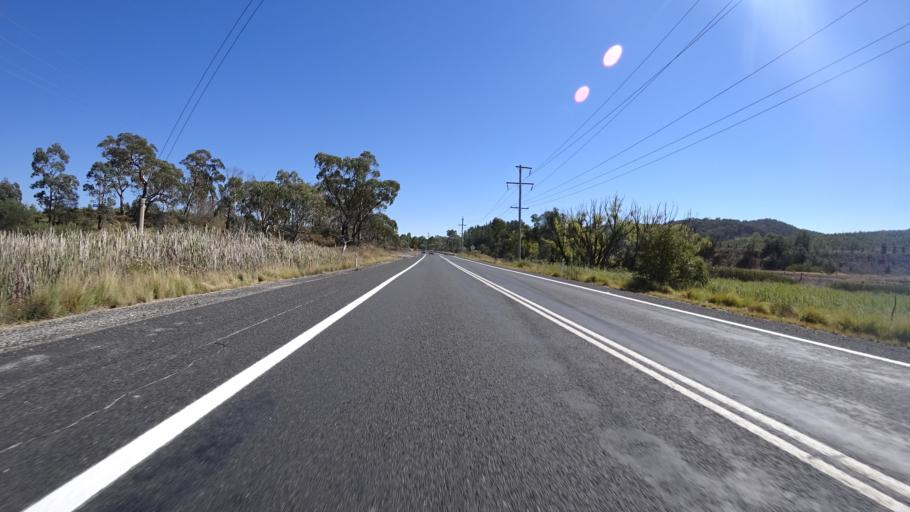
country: AU
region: New South Wales
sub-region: Lithgow
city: Portland
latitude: -33.3625
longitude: 150.0580
